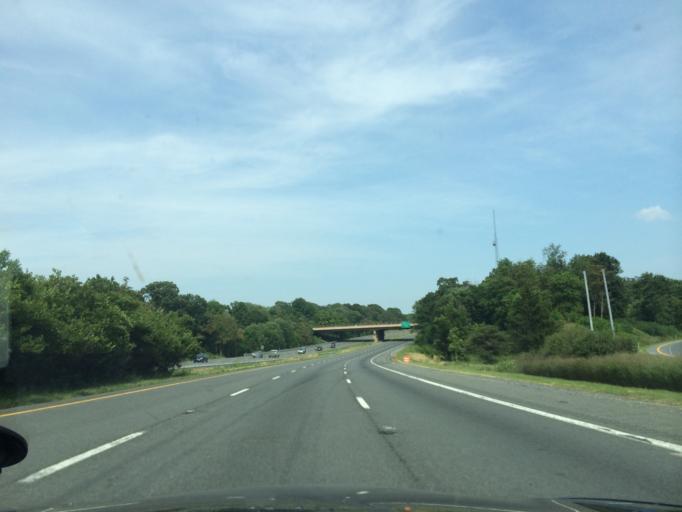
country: US
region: Maryland
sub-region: Frederick County
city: Green Valley
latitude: 39.3818
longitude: -77.2644
